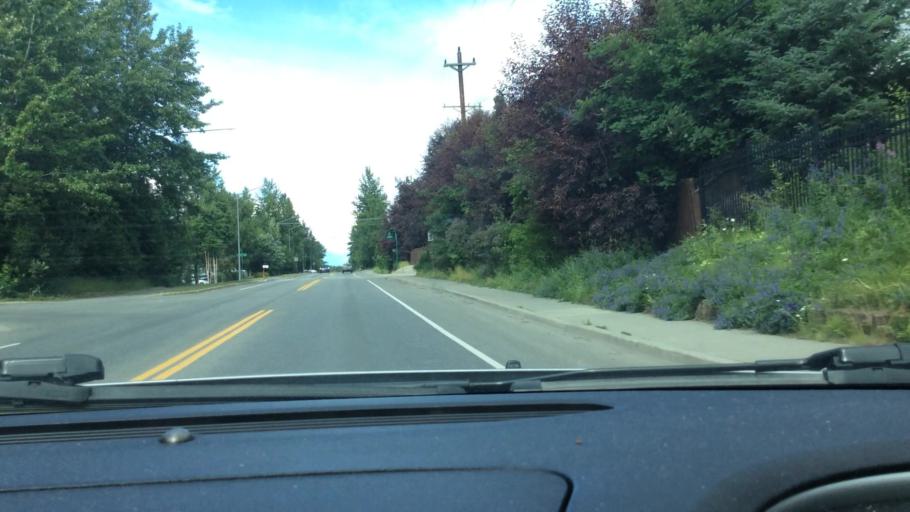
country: US
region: Alaska
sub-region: Anchorage Municipality
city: Elmendorf Air Force Base
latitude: 61.2155
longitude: -149.7559
